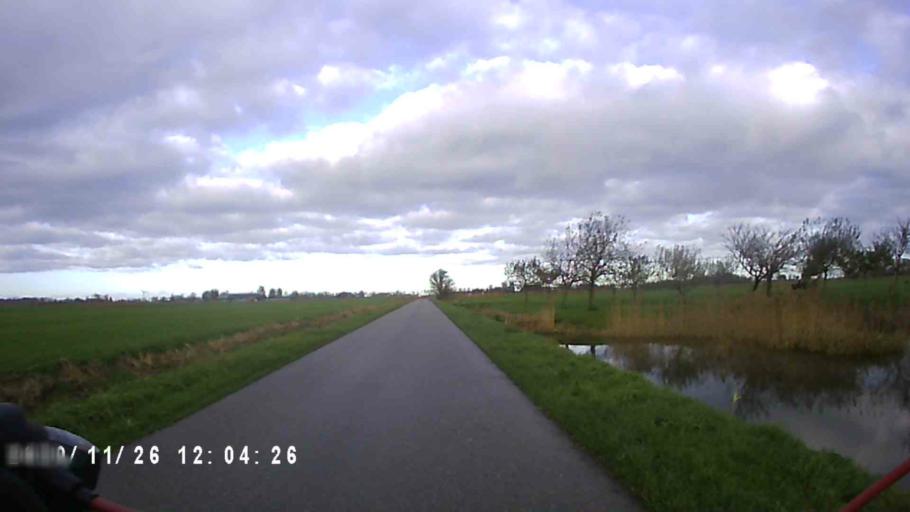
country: NL
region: Groningen
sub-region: Gemeente Bedum
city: Bedum
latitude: 53.3297
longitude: 6.6191
